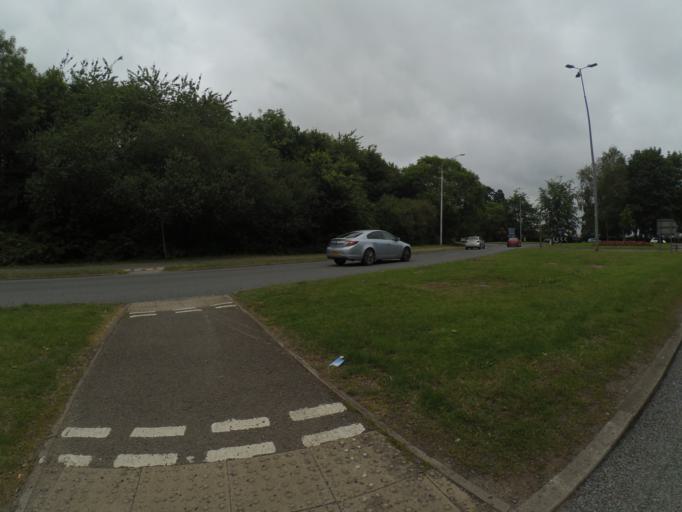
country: GB
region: England
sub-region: Warwickshire
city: Dunchurch
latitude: 52.3467
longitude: -1.2775
